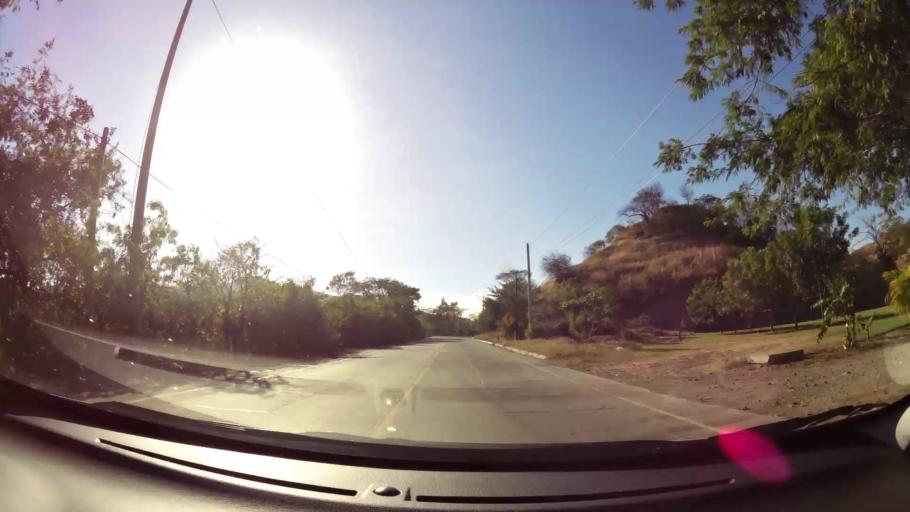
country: SV
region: Santa Ana
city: Texistepeque
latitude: 14.1382
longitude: -89.5111
